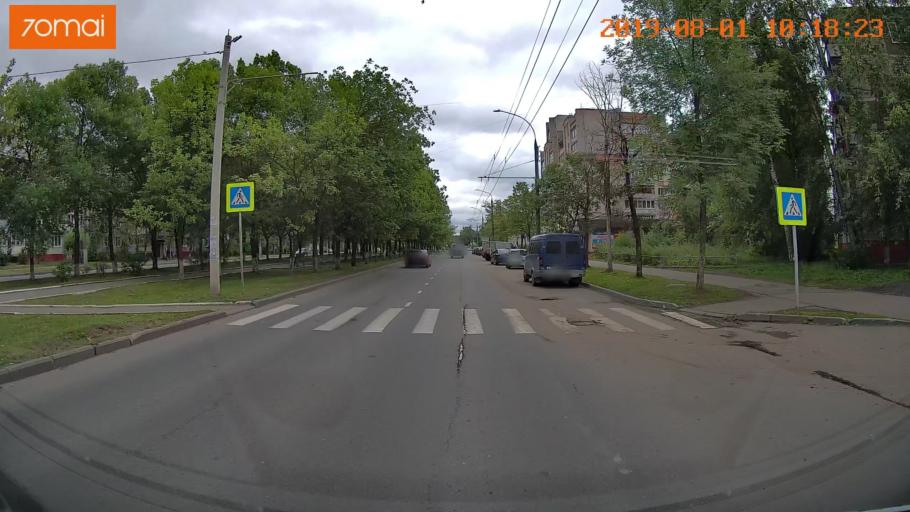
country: RU
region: Ivanovo
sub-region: Gorod Ivanovo
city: Ivanovo
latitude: 56.9619
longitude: 41.0063
